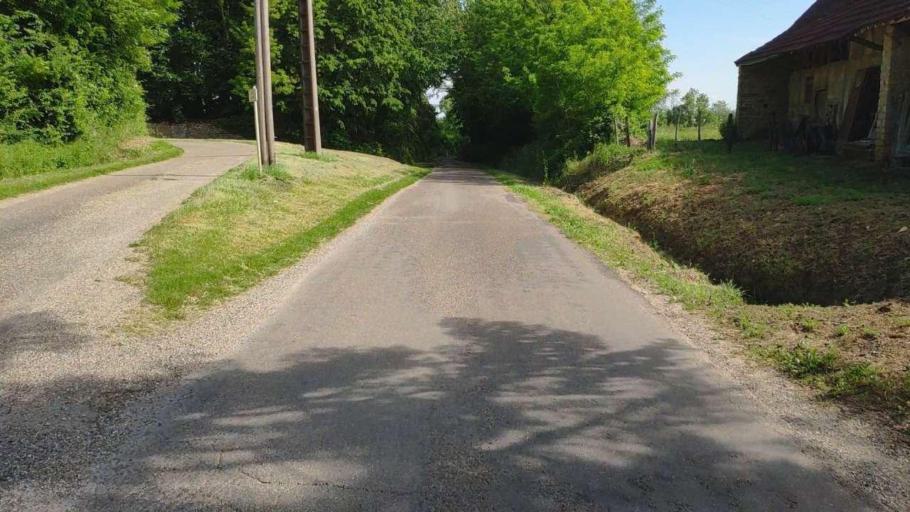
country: FR
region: Franche-Comte
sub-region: Departement du Jura
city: Bletterans
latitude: 46.7142
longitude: 5.4586
